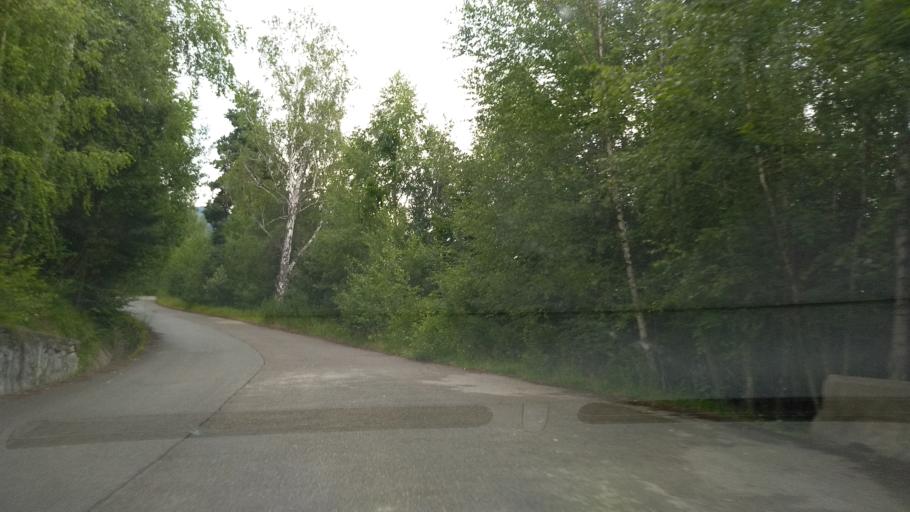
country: RO
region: Hunedoara
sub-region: Municipiul  Vulcan
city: Jiu-Paroseni
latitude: 45.3522
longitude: 23.2889
